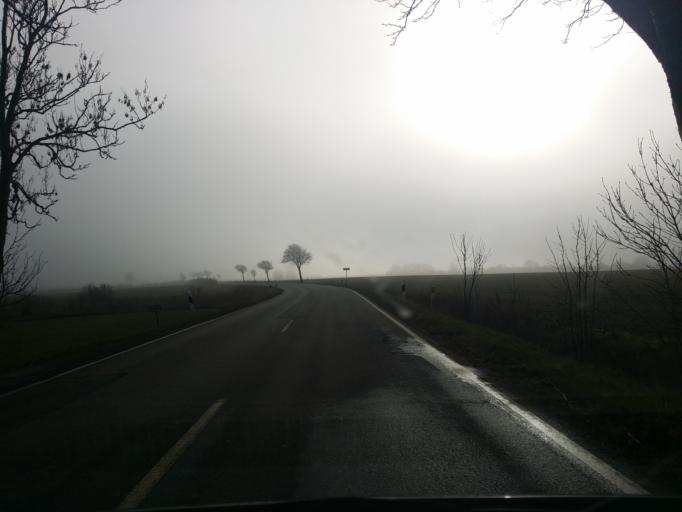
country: DE
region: Schleswig-Holstein
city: Fehmarn
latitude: 54.4430
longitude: 11.1396
